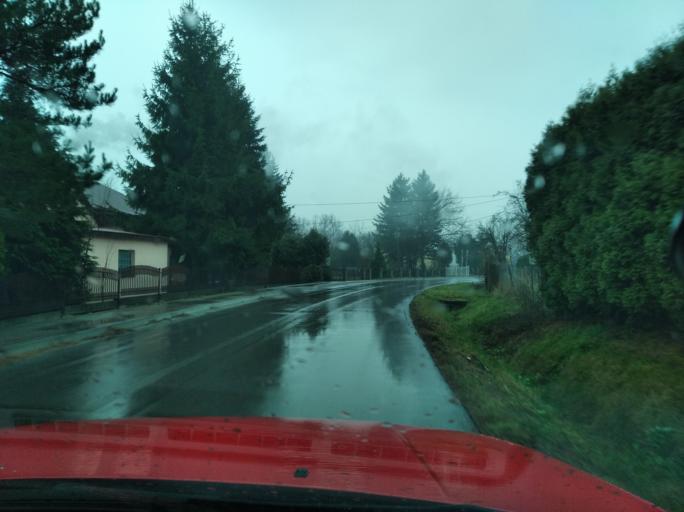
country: PL
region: Subcarpathian Voivodeship
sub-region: Powiat rzeszowski
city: Krasne
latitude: 50.0716
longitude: 22.1227
